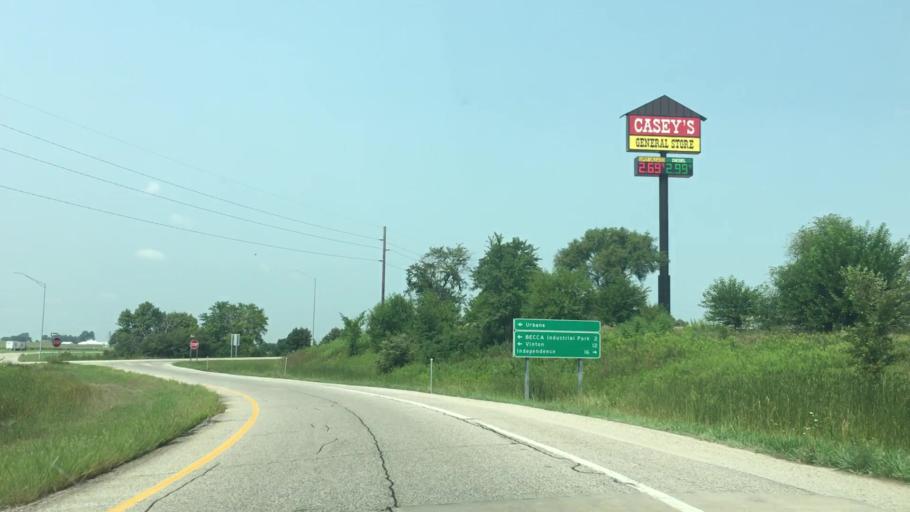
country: US
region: Iowa
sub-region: Benton County
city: Urbana
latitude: 42.2455
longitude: -91.8895
